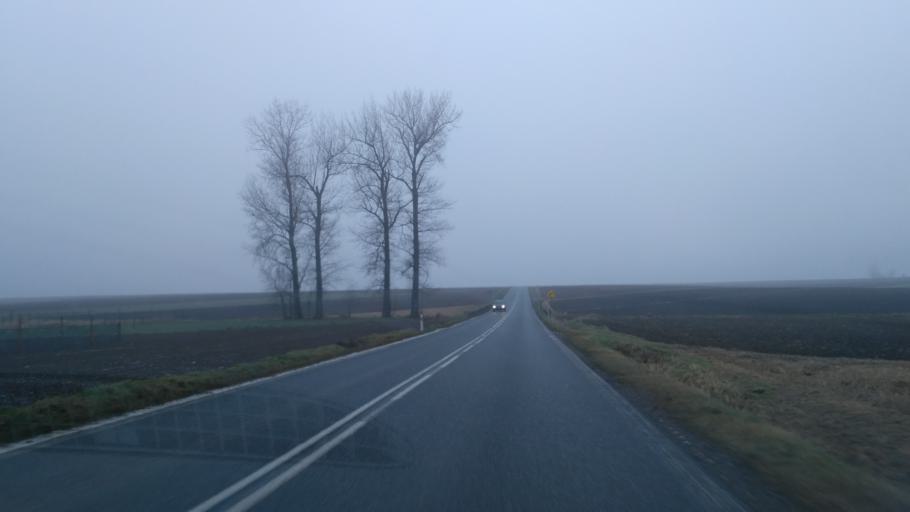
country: PL
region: Subcarpathian Voivodeship
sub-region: Powiat lancucki
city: Markowa
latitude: 50.0352
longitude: 22.3154
